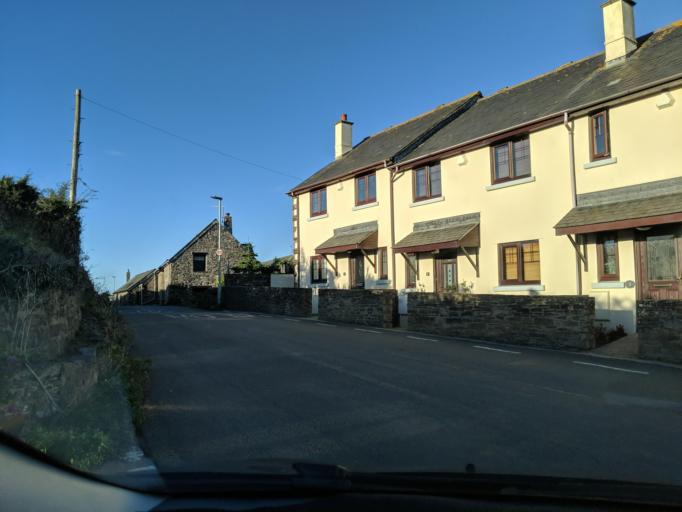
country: GB
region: England
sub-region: Devon
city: Wembury
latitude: 50.3316
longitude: -4.1037
